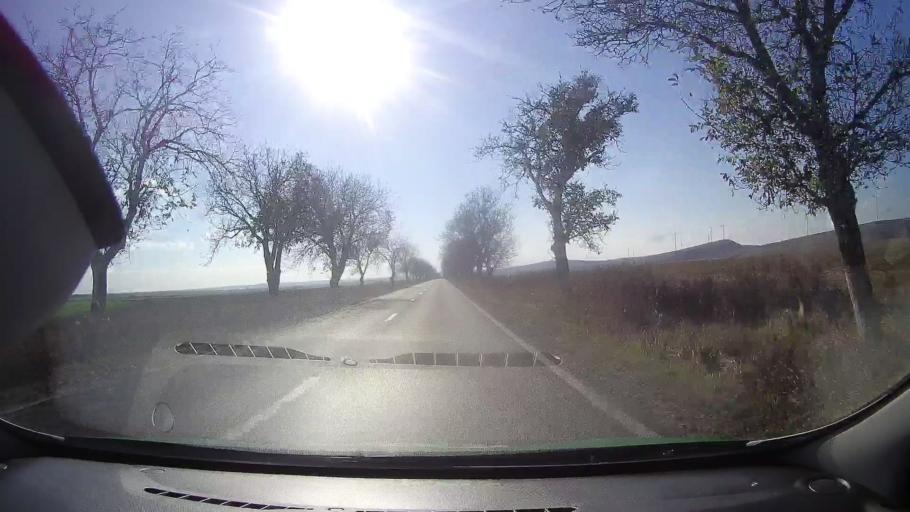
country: RO
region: Tulcea
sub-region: Comuna Ceamurlia de Jos
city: Ceamurlia de Jos
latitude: 44.7908
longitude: 28.6899
